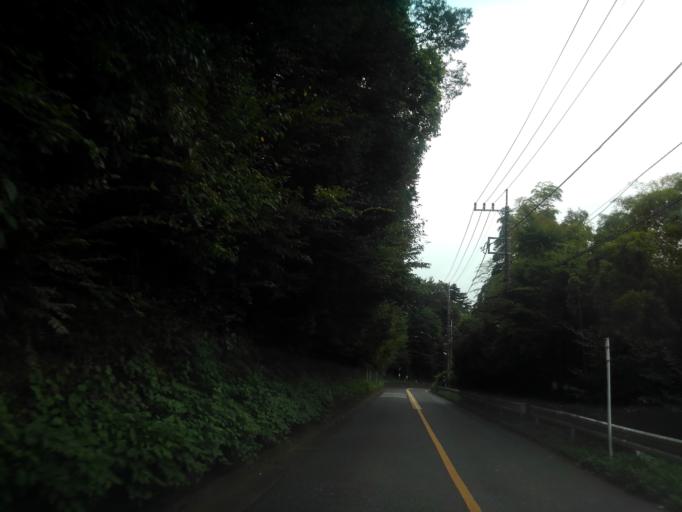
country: JP
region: Tokyo
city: Higashimurayama-shi
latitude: 35.7575
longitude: 139.4161
